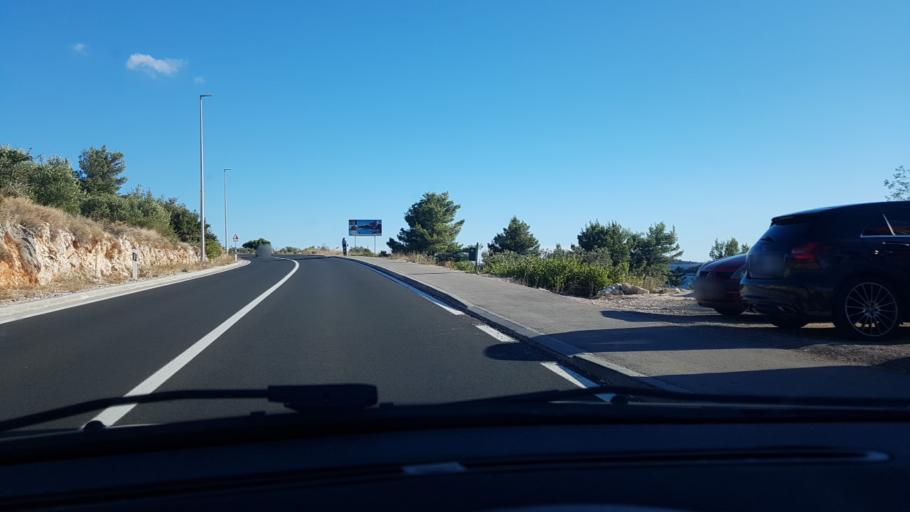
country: HR
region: Sibensko-Kniniska
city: Primosten
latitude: 43.6023
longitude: 15.9221
